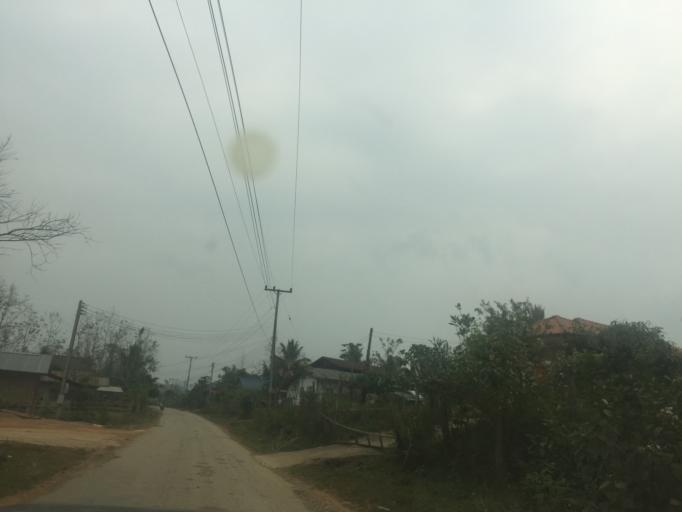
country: LA
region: Vientiane
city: Muang Sanakham
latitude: 18.3875
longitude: 101.5261
